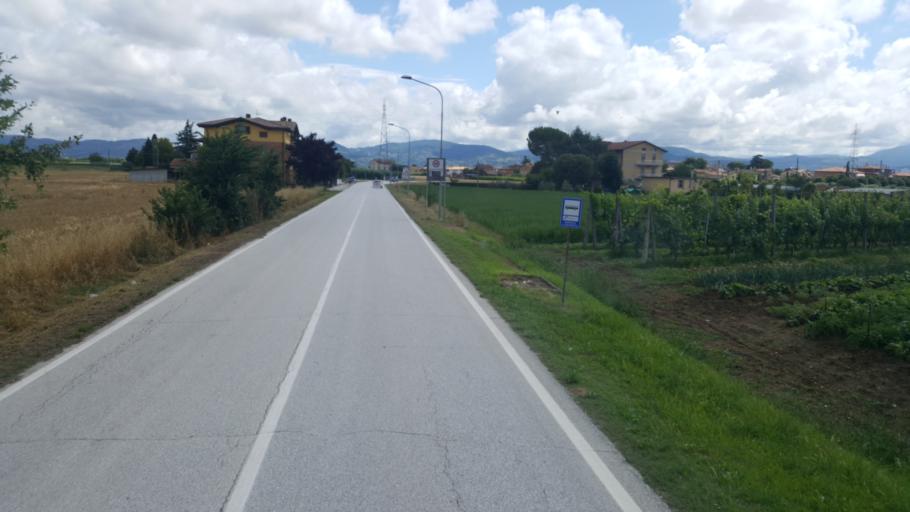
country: IT
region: Umbria
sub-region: Provincia di Perugia
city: Ospedalicchio
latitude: 43.0631
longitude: 12.5056
